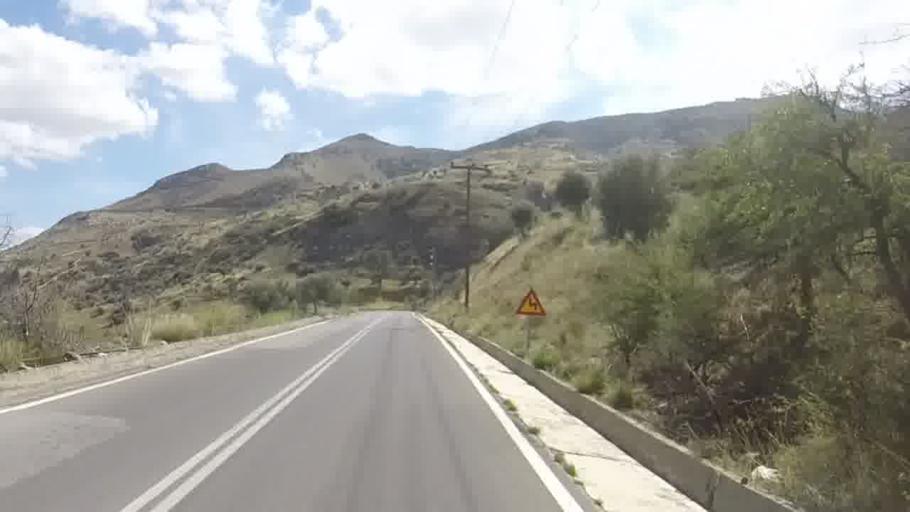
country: GR
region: Crete
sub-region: Nomos Rethymnis
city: Agia Galini
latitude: 35.1437
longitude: 24.6347
